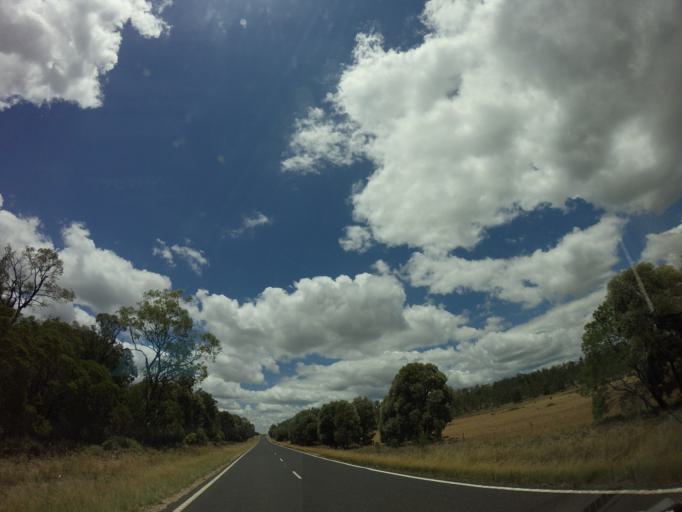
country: AU
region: Queensland
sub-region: Goondiwindi
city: Goondiwindi
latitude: -28.0364
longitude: 150.8128
